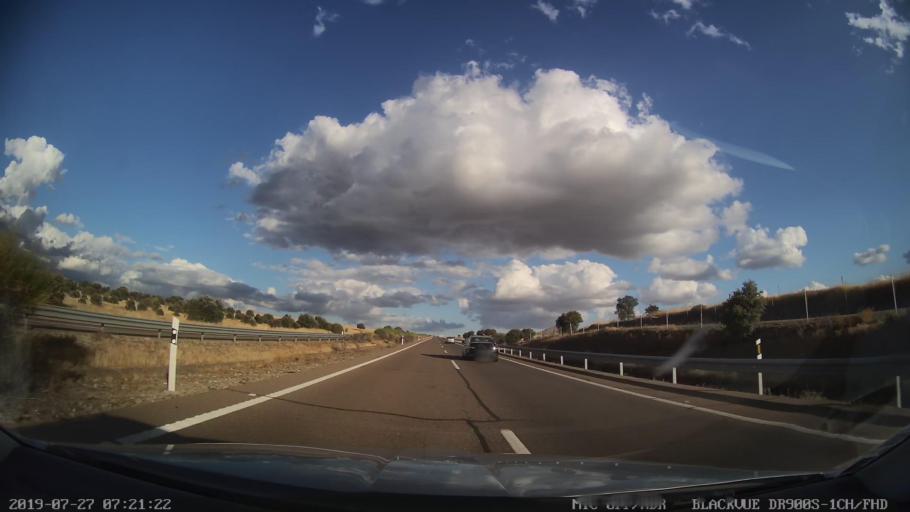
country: ES
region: Extremadura
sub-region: Provincia de Caceres
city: Santa Cruz de la Sierra
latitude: 39.3637
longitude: -5.8707
